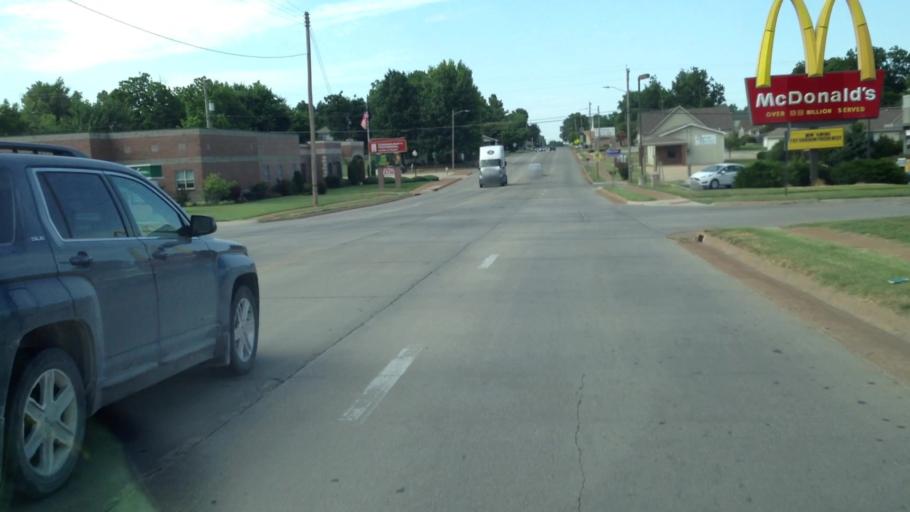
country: US
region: Kansas
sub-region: Labette County
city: Parsons
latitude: 37.3422
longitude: -95.2591
